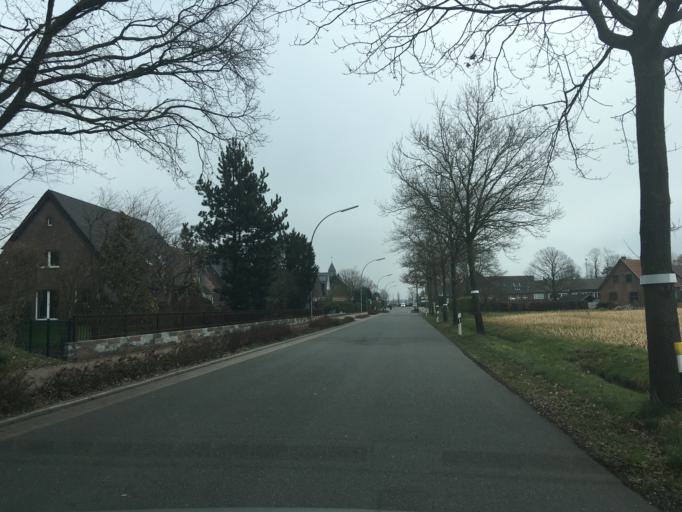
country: DE
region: North Rhine-Westphalia
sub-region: Regierungsbezirk Munster
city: Rhede
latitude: 51.8651
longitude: 6.7328
